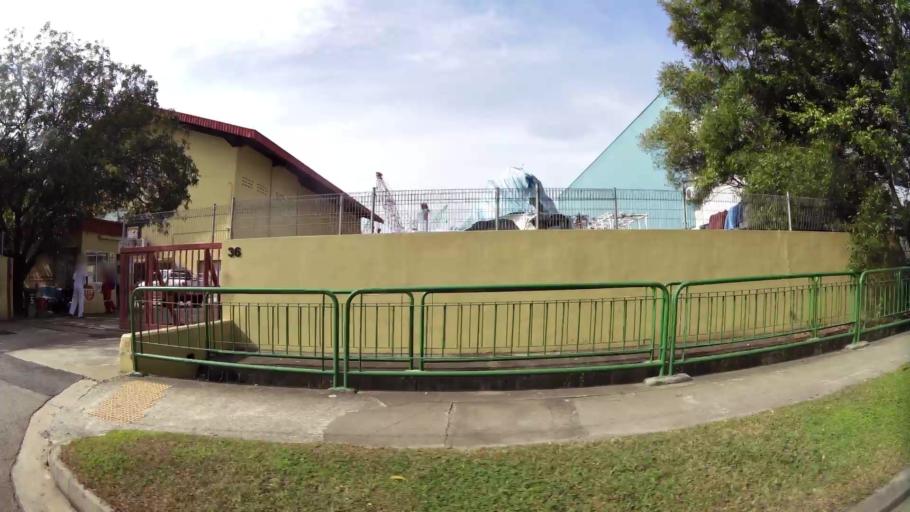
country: MY
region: Johor
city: Johor Bahru
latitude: 1.3165
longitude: 103.6521
